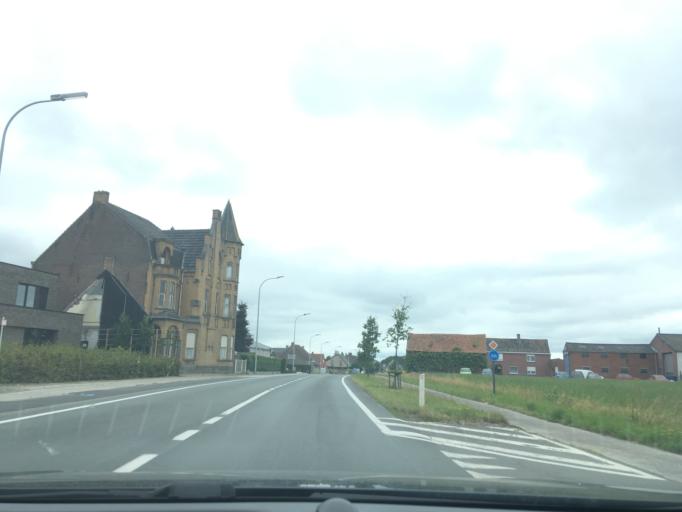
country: BE
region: Flanders
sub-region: Provincie West-Vlaanderen
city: Tielt
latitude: 51.0131
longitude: 3.3150
